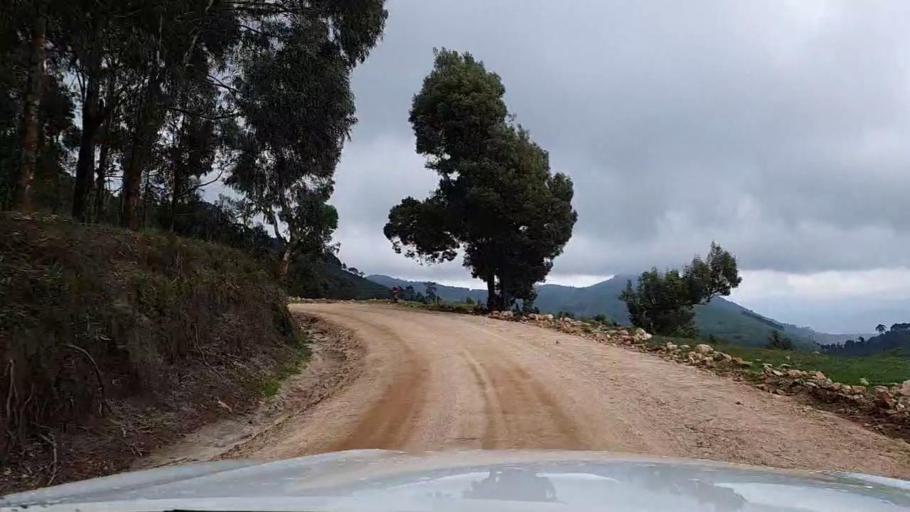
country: RW
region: Southern Province
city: Nzega
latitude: -2.3045
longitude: 29.3836
